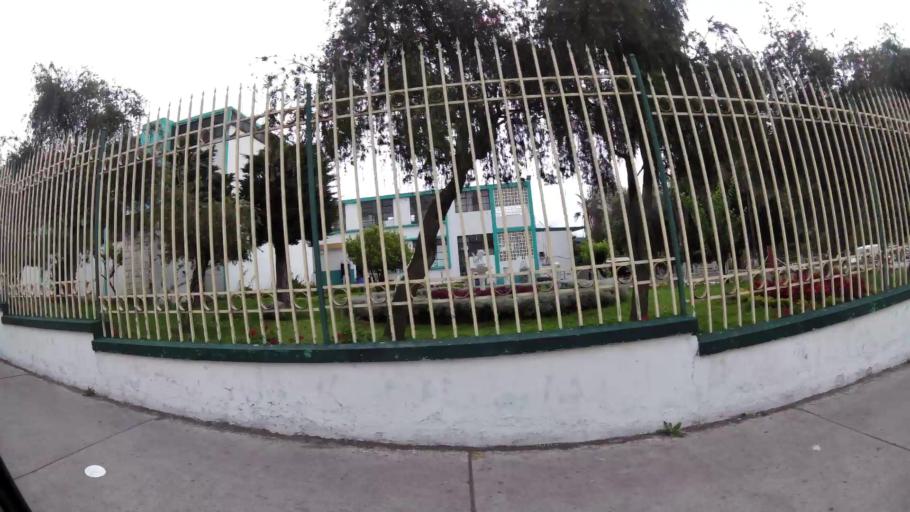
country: EC
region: Tungurahua
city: Ambato
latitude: -1.2539
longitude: -78.6248
